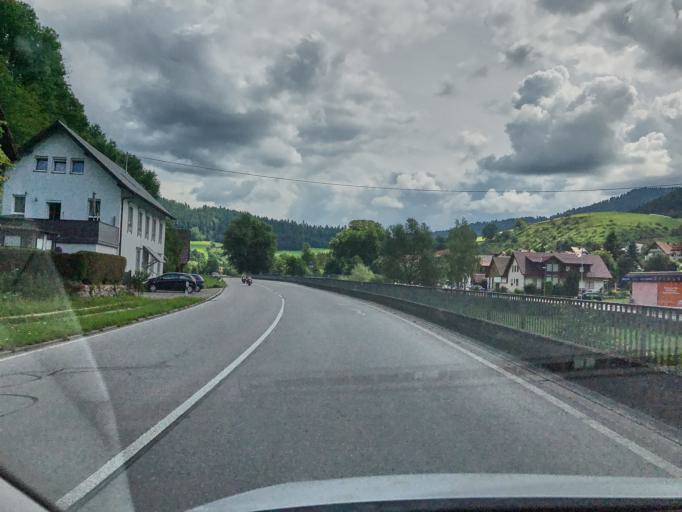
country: DE
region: Baden-Wuerttemberg
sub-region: Freiburg Region
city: Wolfach
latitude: 48.2907
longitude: 8.2640
